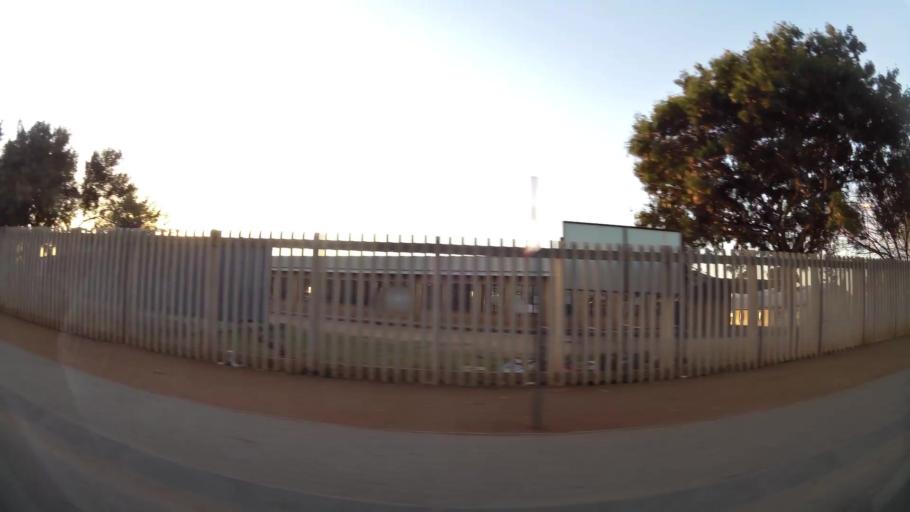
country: ZA
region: Gauteng
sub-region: Ekurhuleni Metropolitan Municipality
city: Tembisa
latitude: -25.9925
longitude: 28.2202
